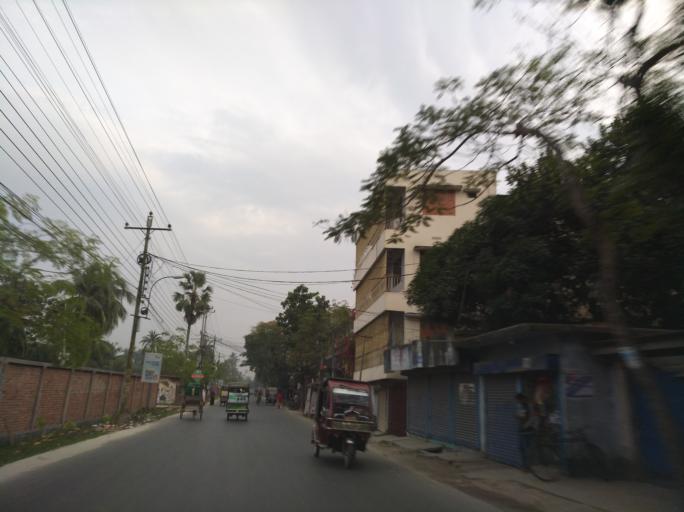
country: BD
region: Khulna
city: Khulna
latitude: 22.8345
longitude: 89.5489
